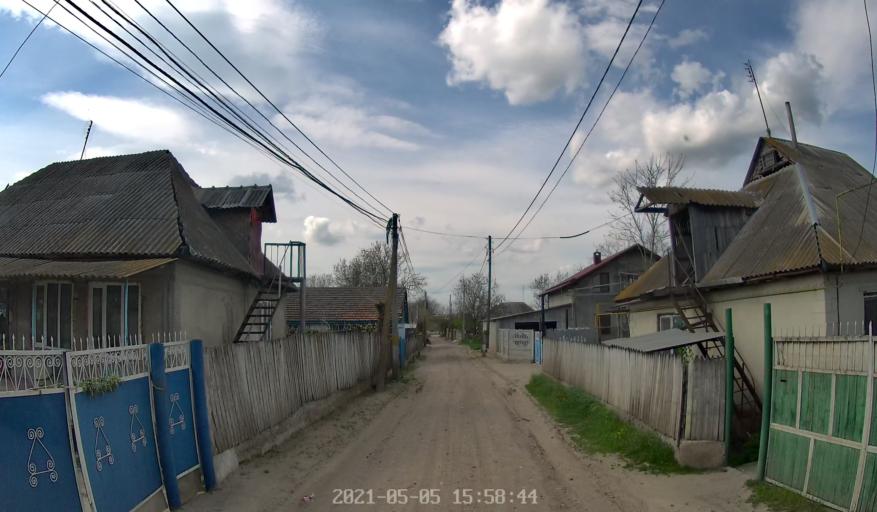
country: MD
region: Criuleni
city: Criuleni
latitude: 47.1389
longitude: 29.2034
